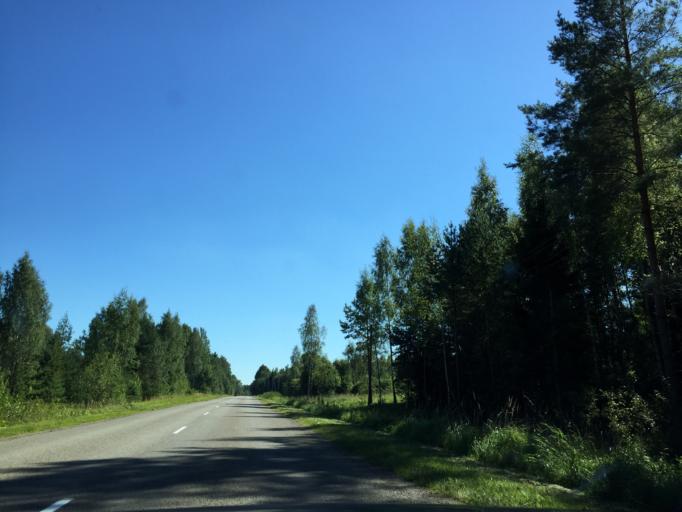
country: LV
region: Akniste
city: Akniste
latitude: 56.0849
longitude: 25.8755
